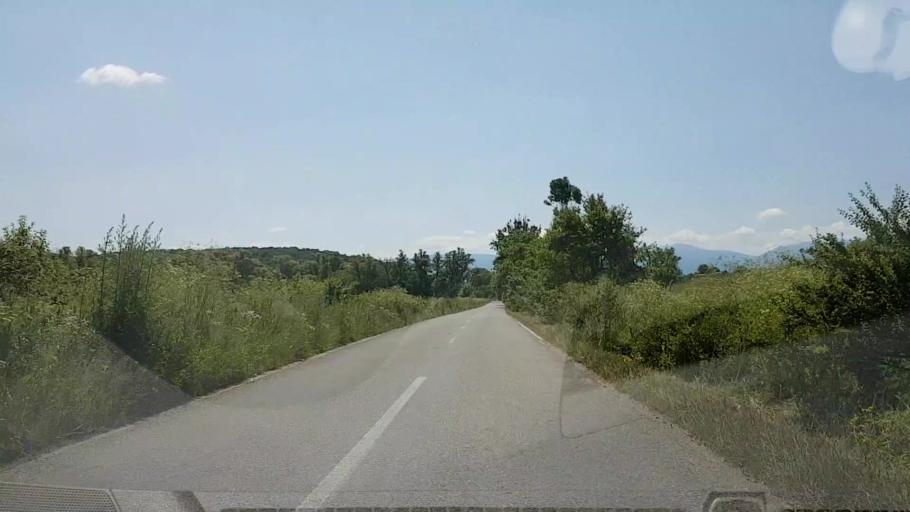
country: RO
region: Brasov
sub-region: Comuna Voila
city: Voila
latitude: 45.8581
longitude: 24.8280
